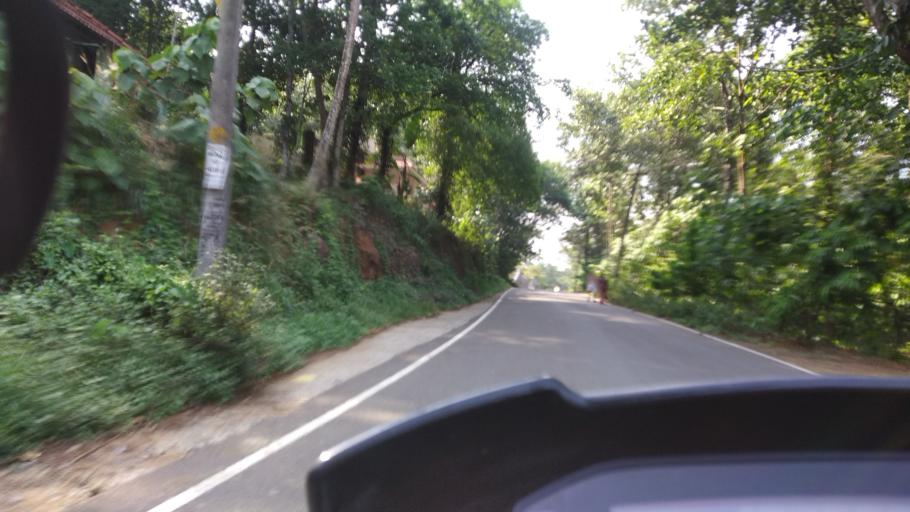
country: IN
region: Kerala
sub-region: Ernakulam
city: Piravam
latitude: 9.8233
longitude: 76.5497
